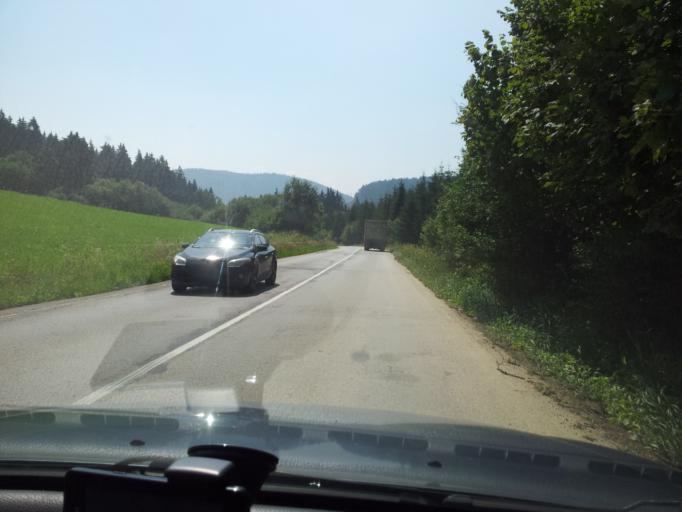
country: SK
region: Zilinsky
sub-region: Okres Dolny Kubin
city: Dolny Kubin
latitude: 49.2787
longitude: 19.3470
